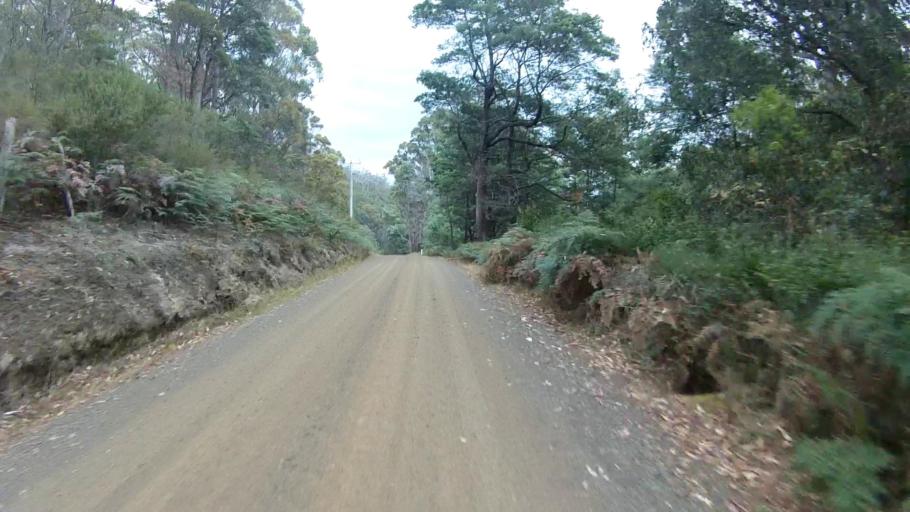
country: AU
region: Tasmania
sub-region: Huon Valley
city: Cygnet
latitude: -43.2241
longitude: 147.1715
